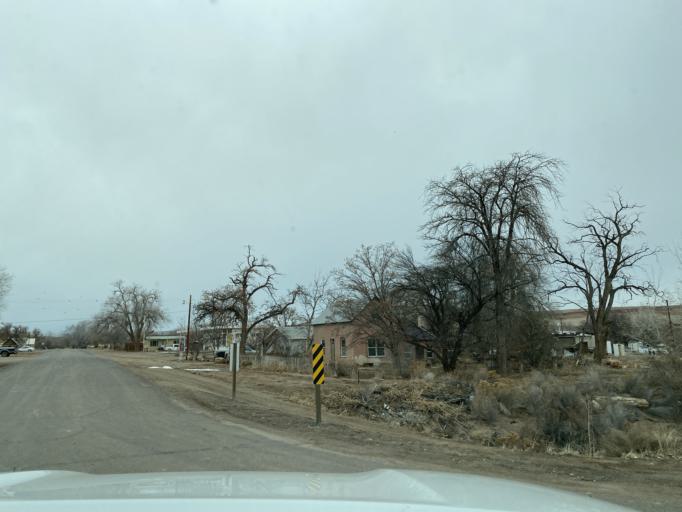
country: US
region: Utah
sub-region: Emery County
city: Ferron
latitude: 38.3728
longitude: -110.7122
